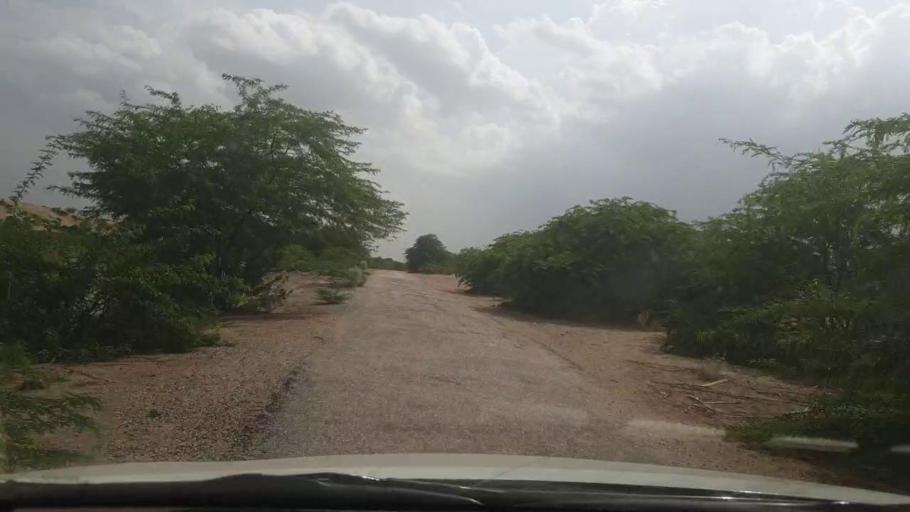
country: PK
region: Sindh
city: Kot Diji
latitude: 27.3432
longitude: 69.0206
